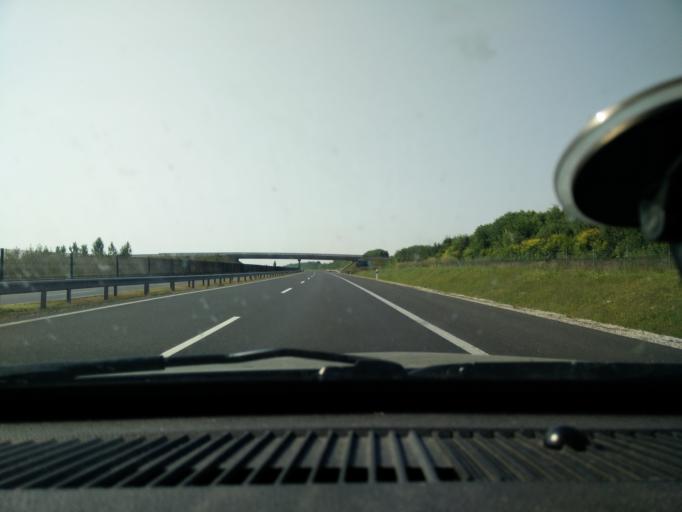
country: HU
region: Fejer
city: Ivancsa
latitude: 47.1515
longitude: 18.8048
